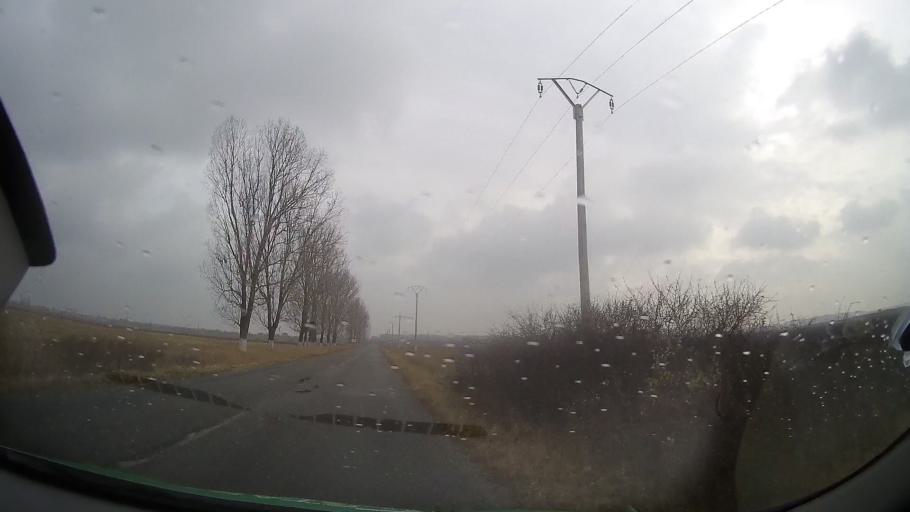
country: RO
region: Prahova
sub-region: Comuna Draganesti
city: Draganesti
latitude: 44.8333
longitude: 26.2722
